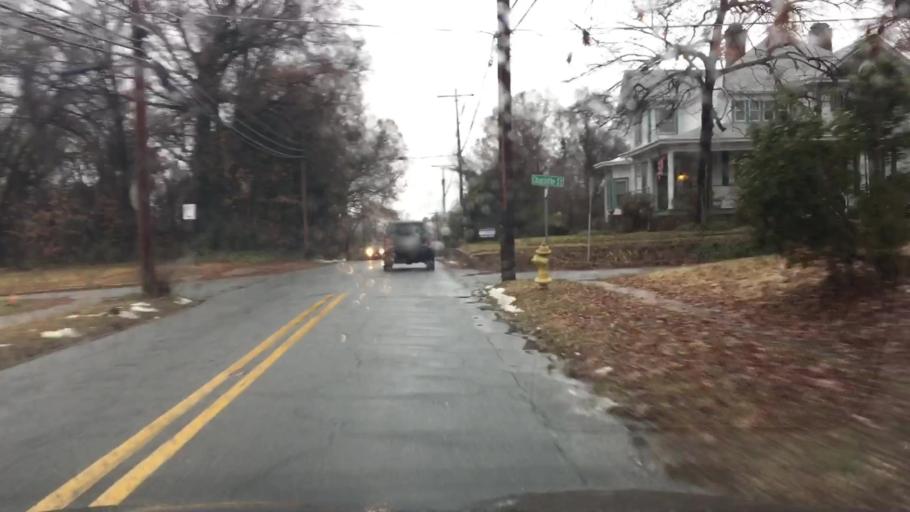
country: US
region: North Carolina
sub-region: Iredell County
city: Mooresville
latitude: 35.5848
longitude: -80.8175
